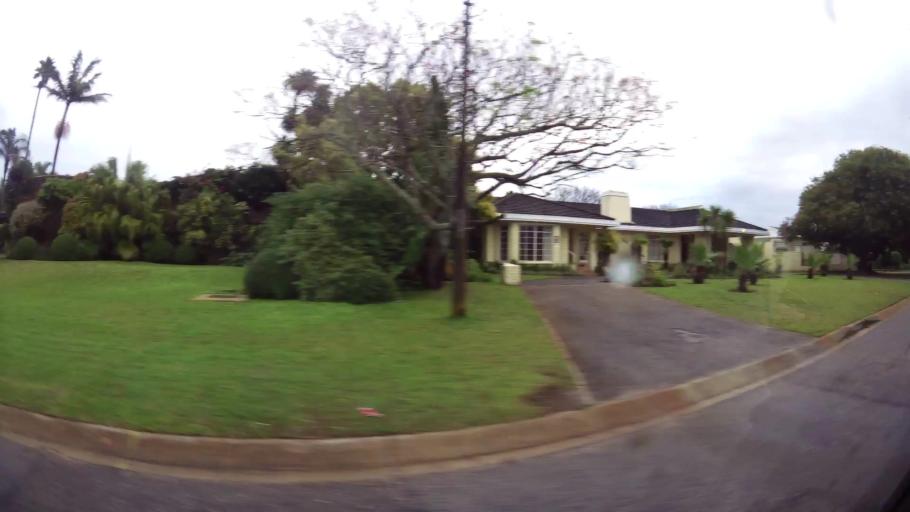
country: ZA
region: Eastern Cape
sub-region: Nelson Mandela Bay Metropolitan Municipality
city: Port Elizabeth
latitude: -33.9762
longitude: 25.5659
